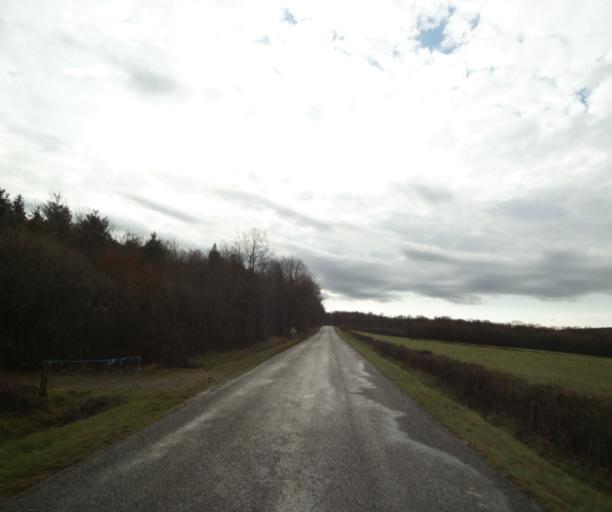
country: FR
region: Auvergne
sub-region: Departement de l'Allier
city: Neuilly-le-Real
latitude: 46.5200
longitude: 3.4225
